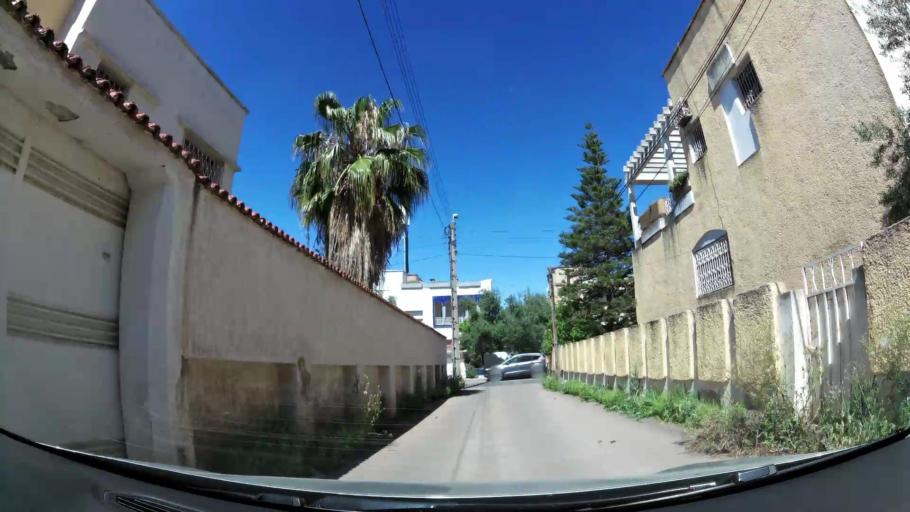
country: MA
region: Fes-Boulemane
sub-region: Fes
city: Fes
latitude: 34.0174
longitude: -4.9916
